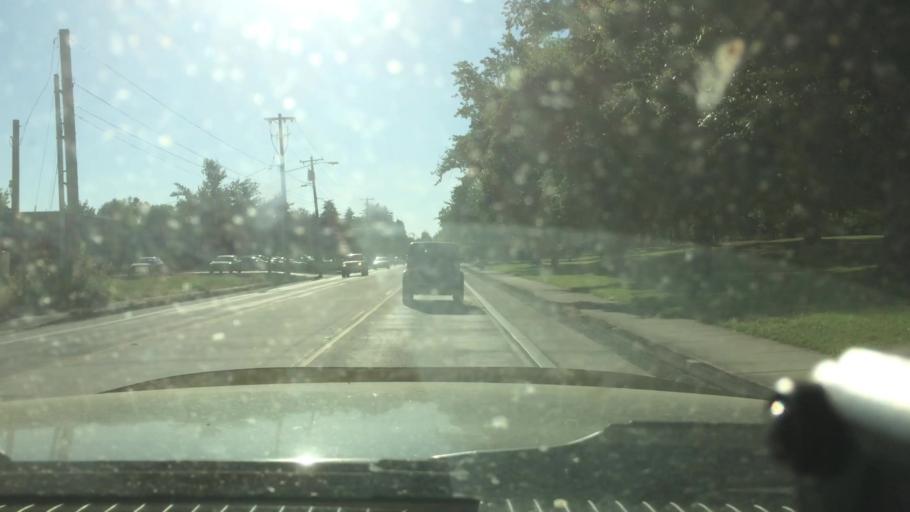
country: US
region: Oregon
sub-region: Lane County
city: Eugene
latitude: 44.0404
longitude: -123.1157
